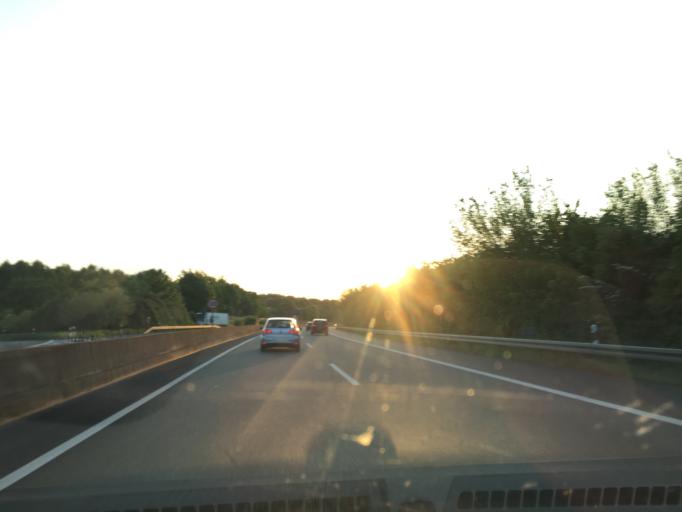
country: DE
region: Lower Saxony
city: Osnabrueck
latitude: 52.2445
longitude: 8.0355
